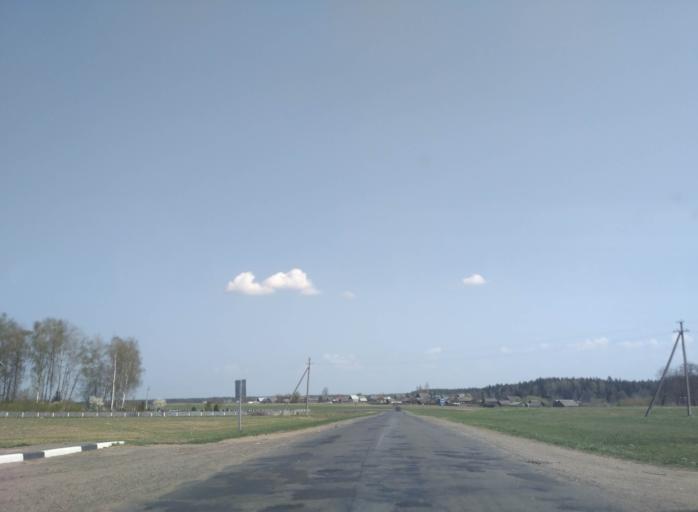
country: BY
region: Minsk
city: Horad Barysaw
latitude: 54.3157
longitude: 28.5584
